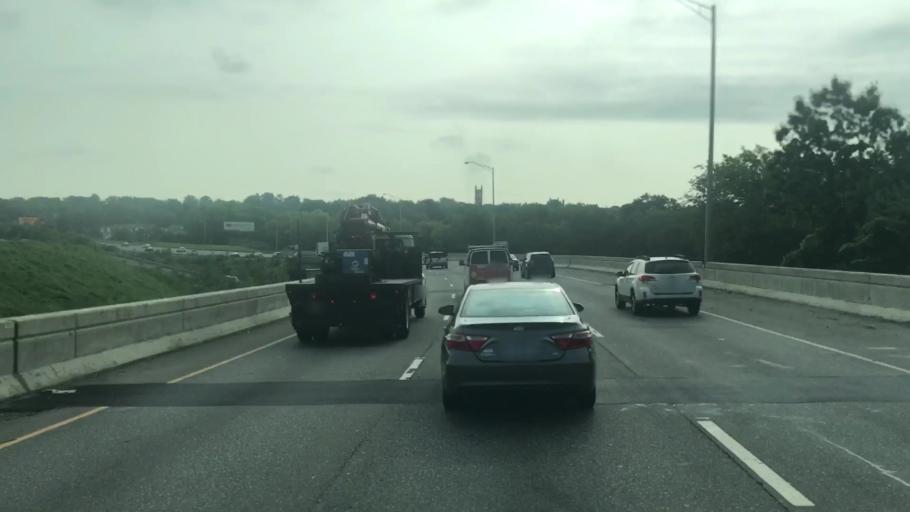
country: US
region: Connecticut
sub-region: Hartford County
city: Hartford
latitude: 41.7492
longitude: -72.7079
